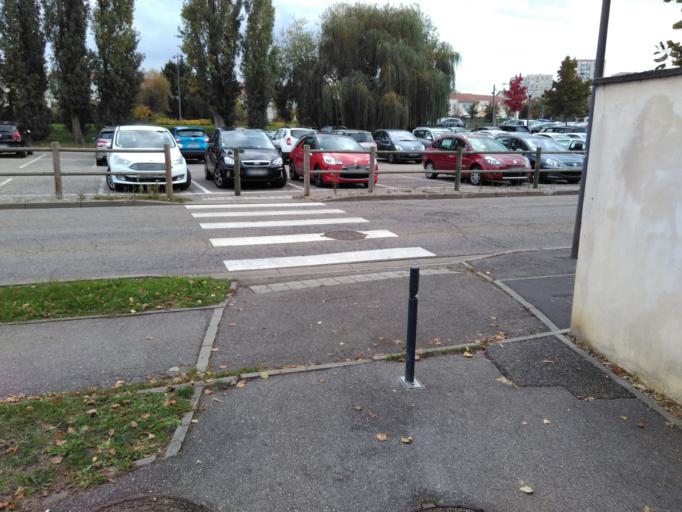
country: FR
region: Lorraine
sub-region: Departement de Meurthe-et-Moselle
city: Essey-les-Nancy
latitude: 48.7028
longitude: 6.2256
